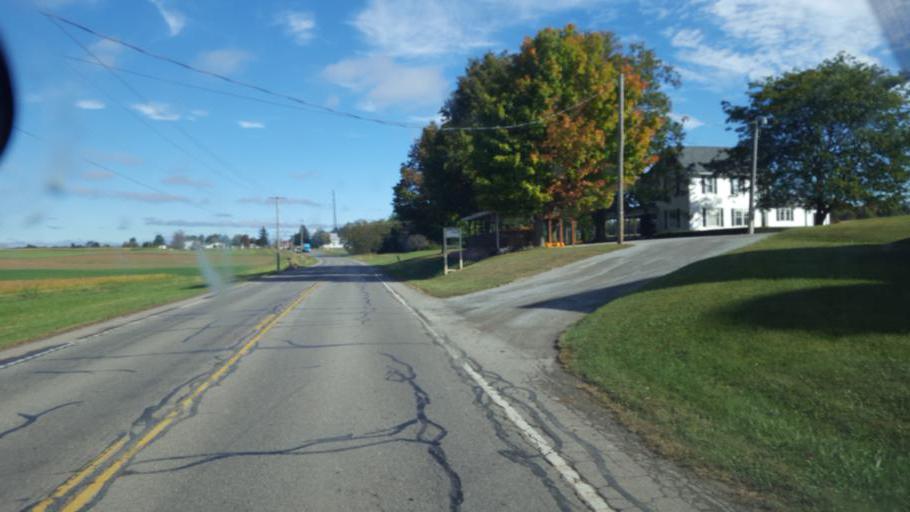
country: US
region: Ohio
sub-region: Huron County
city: Greenwich
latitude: 40.9044
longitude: -82.5001
